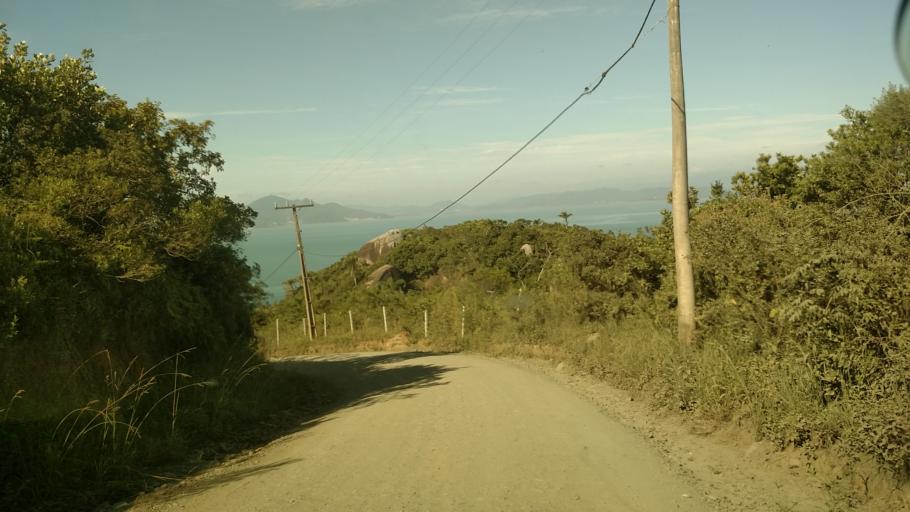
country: BR
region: Santa Catarina
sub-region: Porto Belo
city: Porto Belo
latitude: -27.2117
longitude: -48.5035
